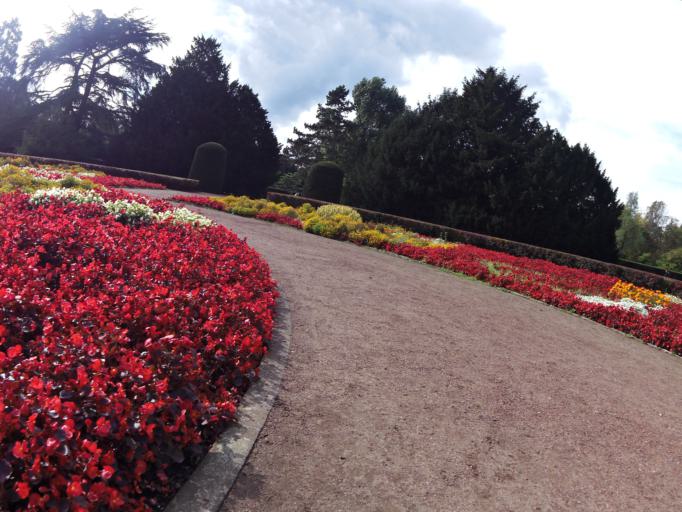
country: DE
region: North Rhine-Westphalia
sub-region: Regierungsbezirk Dusseldorf
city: Dusseldorf
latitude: 51.2570
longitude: 6.7460
